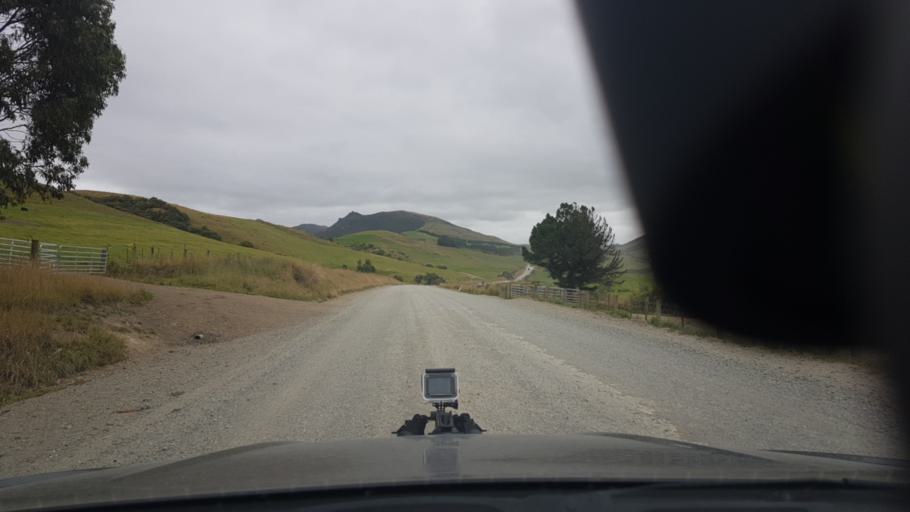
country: NZ
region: Otago
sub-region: Clutha District
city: Papatowai
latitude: -46.3433
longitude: 169.4304
